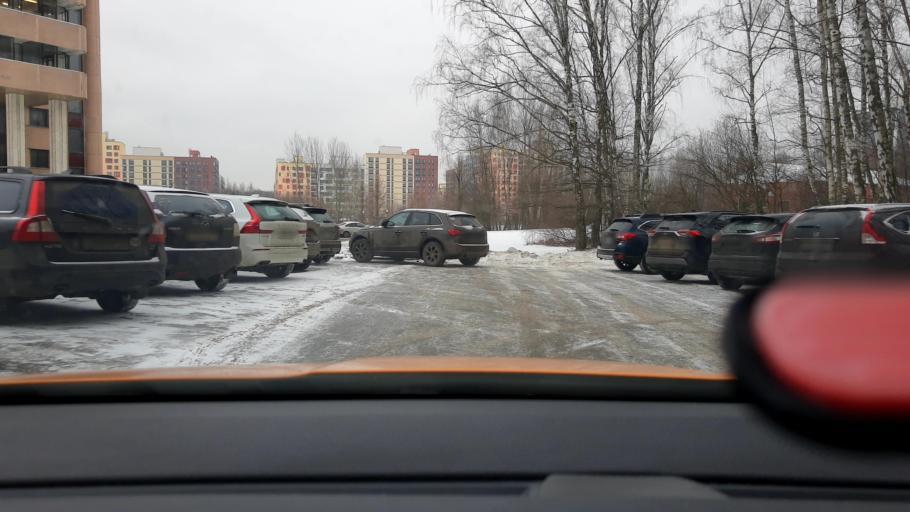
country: RU
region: Moskovskaya
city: Krasnogorsk
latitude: 55.8739
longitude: 37.3220
